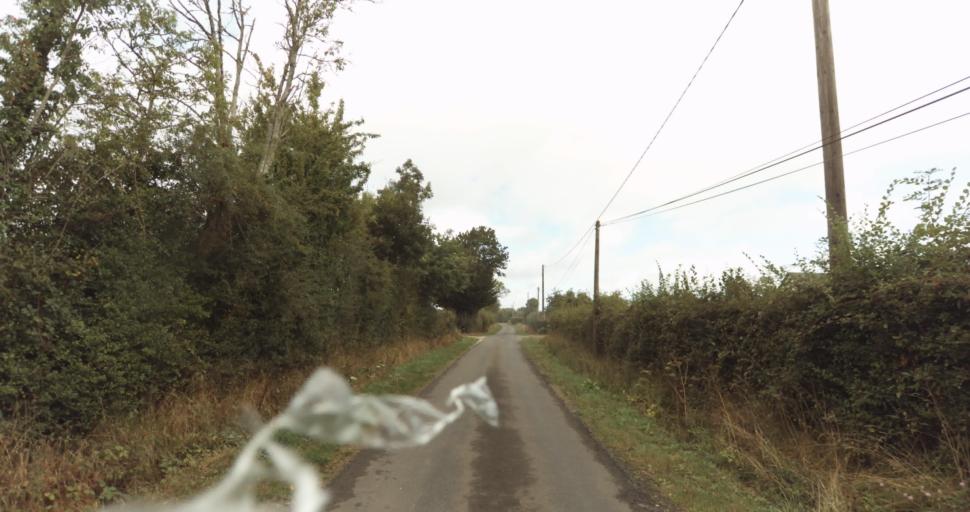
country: FR
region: Lower Normandy
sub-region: Departement de l'Orne
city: Gace
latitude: 48.8489
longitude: 0.3216
